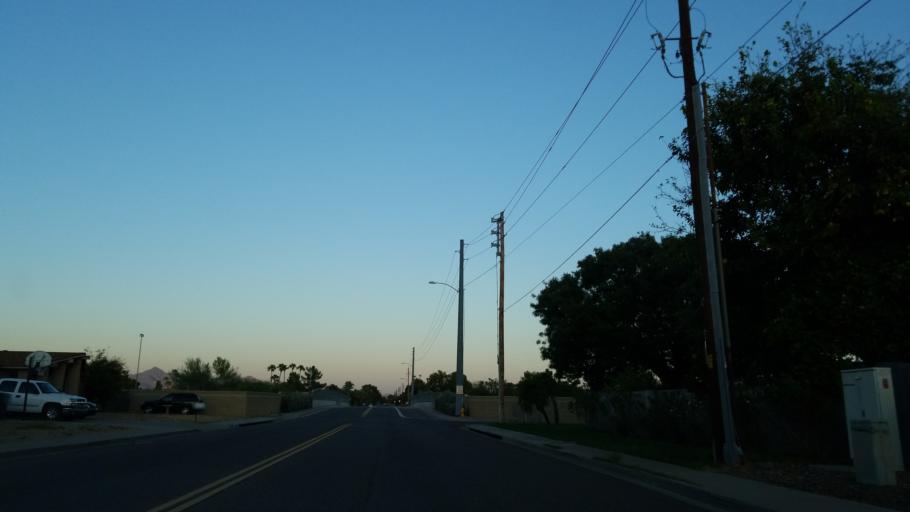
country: US
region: Arizona
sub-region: Maricopa County
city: Paradise Valley
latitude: 33.5898
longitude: -112.0112
